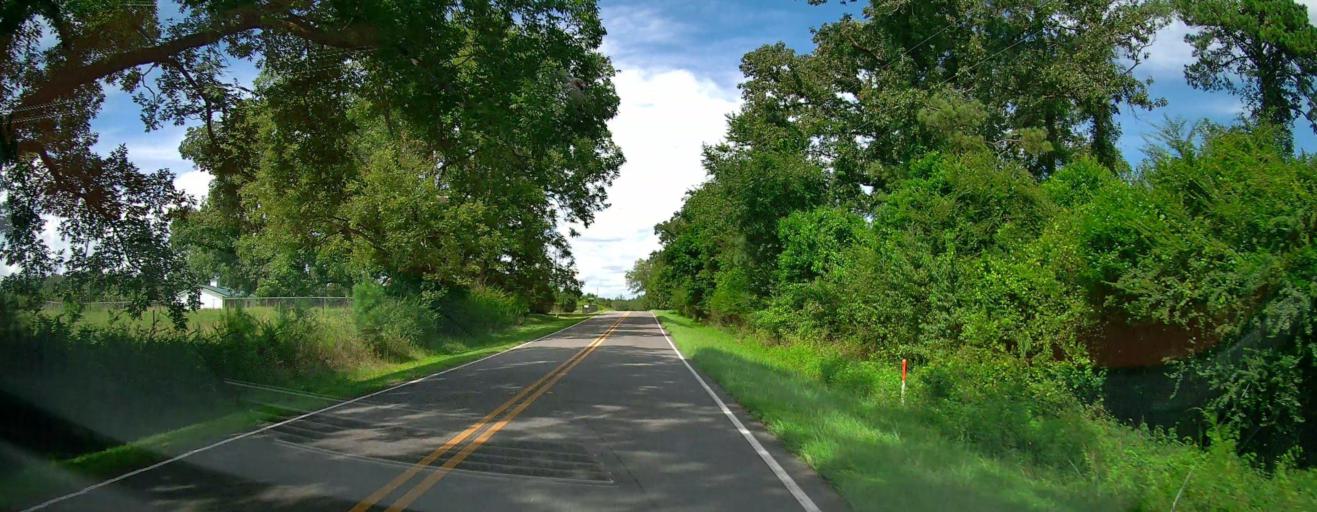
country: US
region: Georgia
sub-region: Taylor County
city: Butler
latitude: 32.4888
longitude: -84.2056
